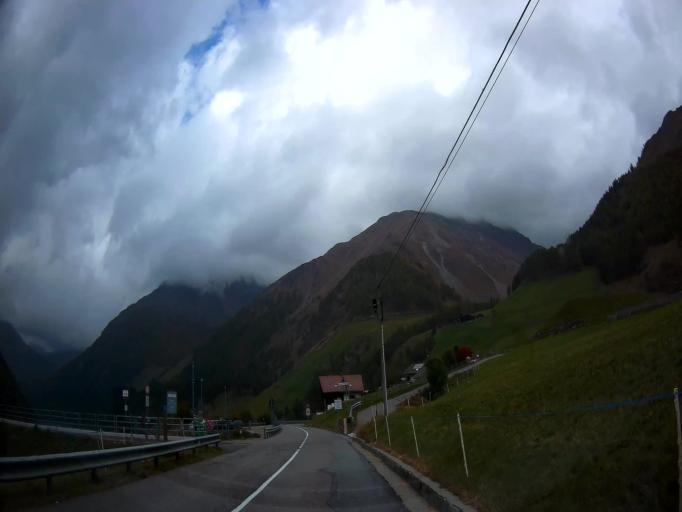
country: IT
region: Trentino-Alto Adige
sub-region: Bolzano
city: Senales
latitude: 46.7348
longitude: 10.8504
